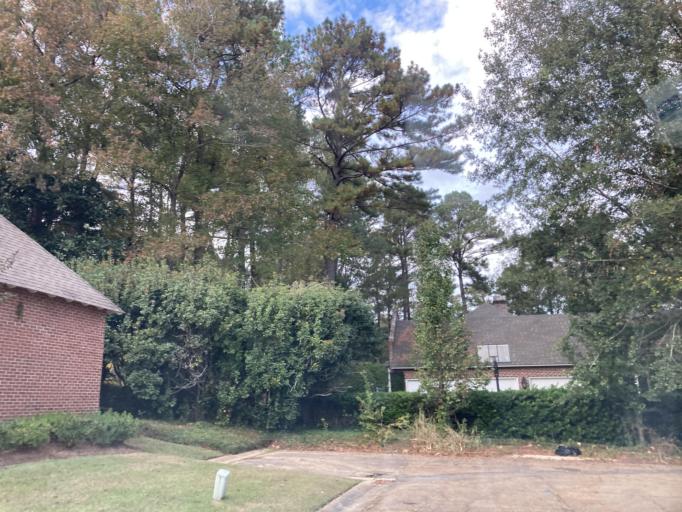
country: US
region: Mississippi
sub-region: Lamar County
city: West Hattiesburg
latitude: 31.3165
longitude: -89.4655
